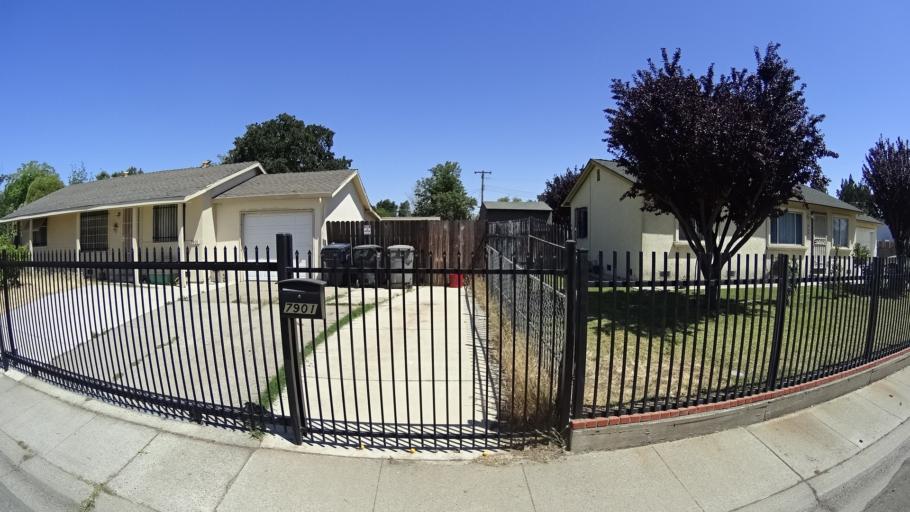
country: US
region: California
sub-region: Sacramento County
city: Florin
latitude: 38.5092
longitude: -121.4110
